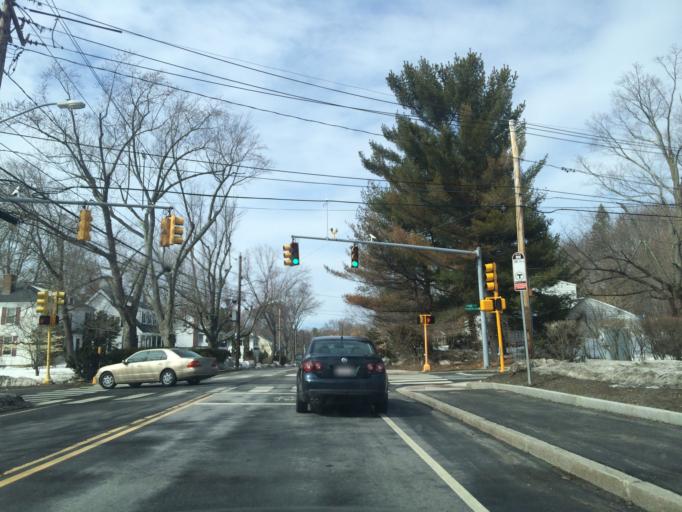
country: US
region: Massachusetts
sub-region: Middlesex County
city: Lexington
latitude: 42.4562
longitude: -71.2354
